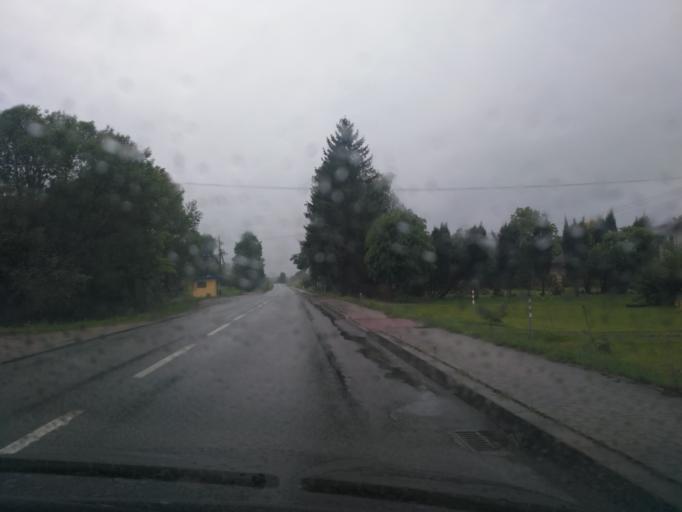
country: PL
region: Subcarpathian Voivodeship
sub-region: Powiat krosnienski
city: Leki
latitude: 49.7998
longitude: 21.6450
